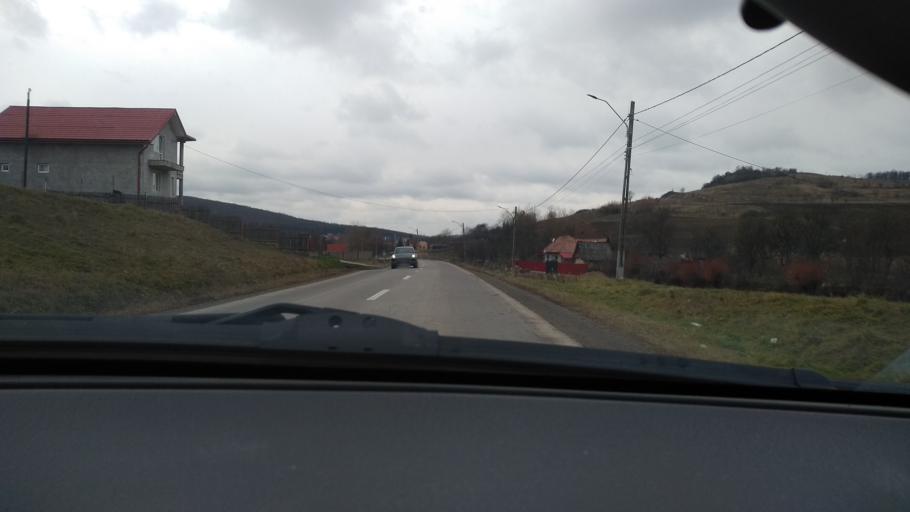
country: RO
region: Mures
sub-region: Comuna Livezeni
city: Livezeni
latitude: 46.5418
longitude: 24.6876
